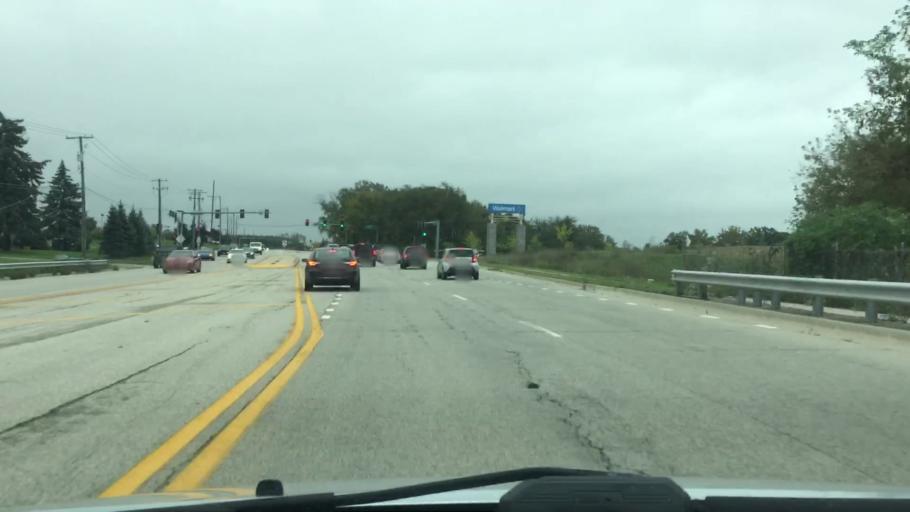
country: US
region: Illinois
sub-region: McHenry County
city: McCullom Lake
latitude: 42.3720
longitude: -88.2694
